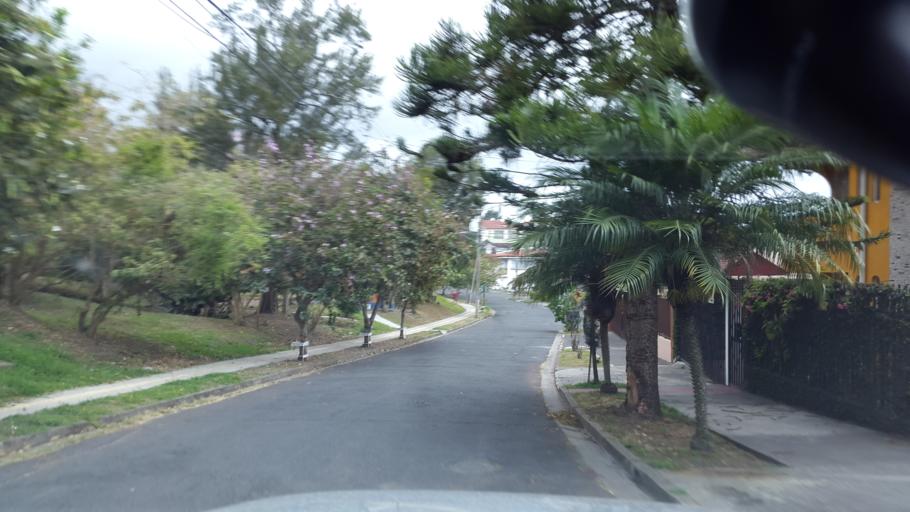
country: CR
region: San Jose
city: San Vicente de Moravia
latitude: 9.9602
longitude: -84.0560
